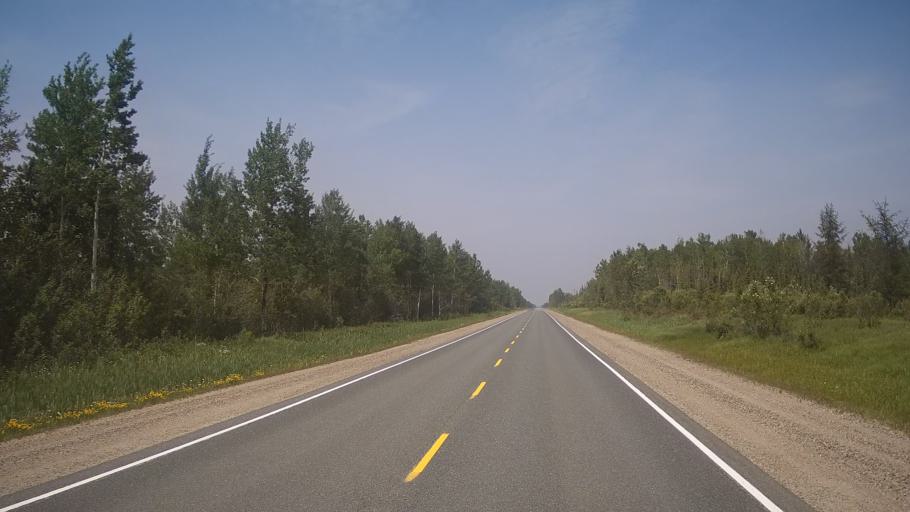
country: CA
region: Ontario
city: Timmins
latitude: 48.8182
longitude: -81.3701
